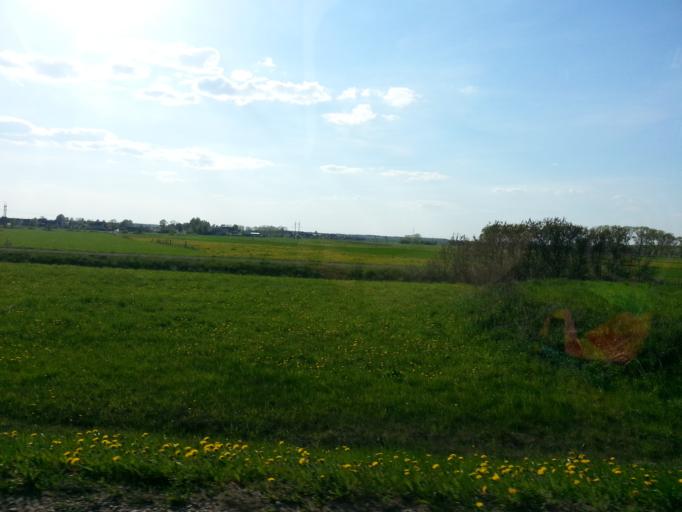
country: LT
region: Panevezys
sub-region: Panevezys City
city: Panevezys
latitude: 55.7819
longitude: 24.3075
